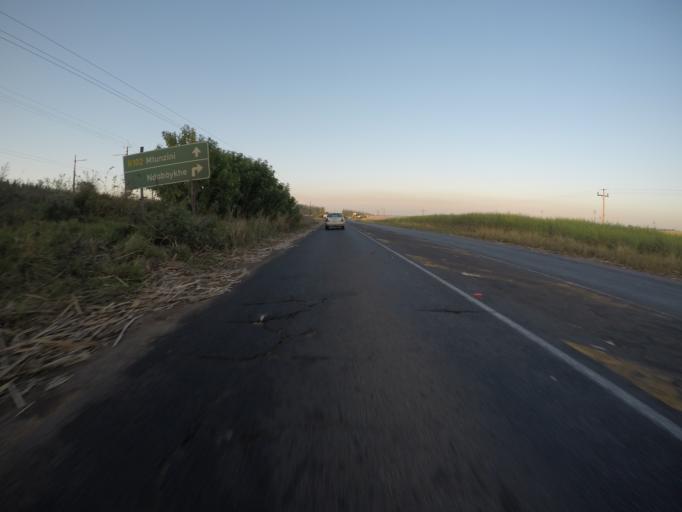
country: ZA
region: KwaZulu-Natal
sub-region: uThungulu District Municipality
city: Empangeni
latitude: -28.8077
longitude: 31.8920
